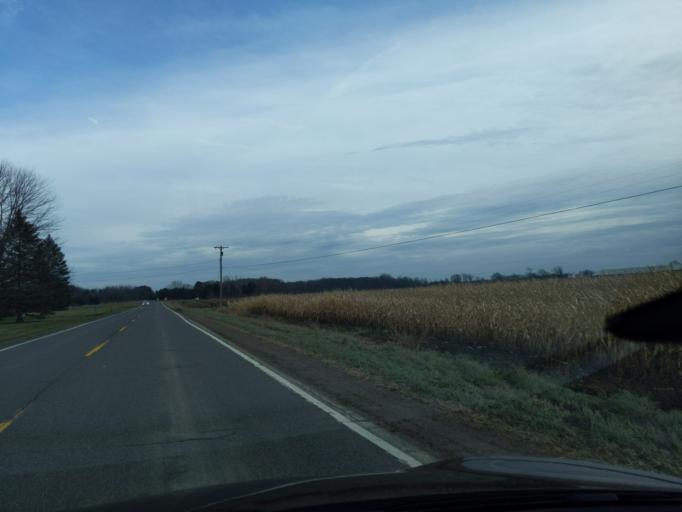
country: US
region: Michigan
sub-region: Ingham County
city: Mason
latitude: 42.6398
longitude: -84.3700
